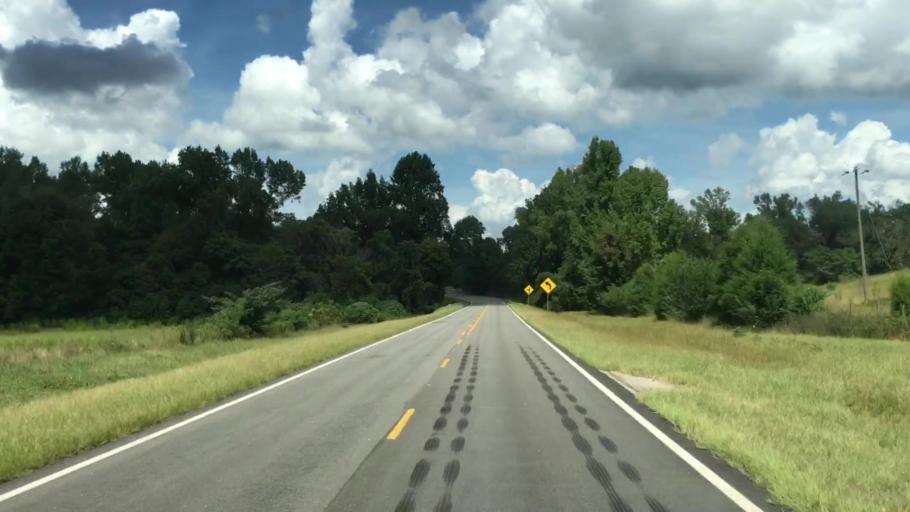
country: US
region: Georgia
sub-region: Greene County
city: Union Point
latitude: 33.5477
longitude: -83.0975
